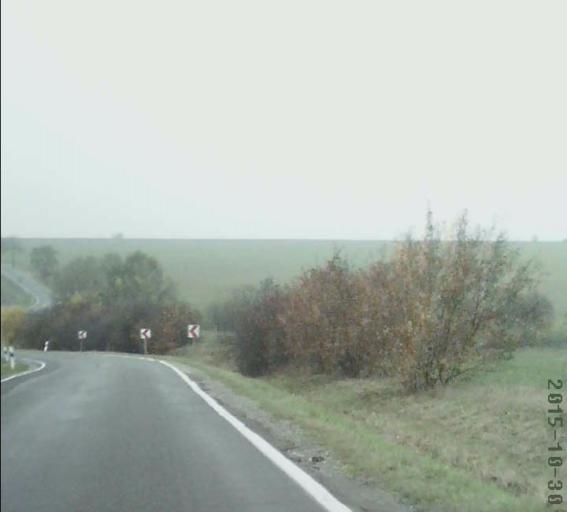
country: DE
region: Thuringia
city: Muehlhausen
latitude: 51.2310
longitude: 10.4070
